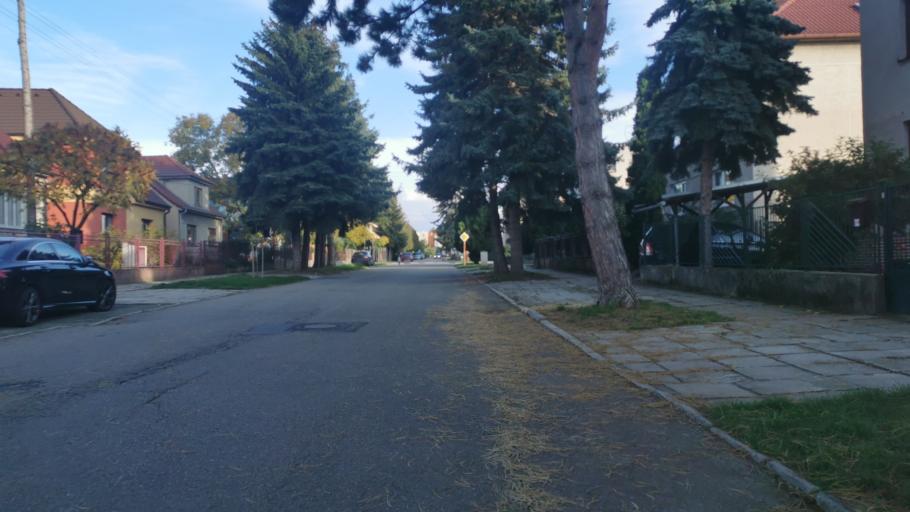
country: SK
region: Trnavsky
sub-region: Okres Skalica
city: Skalica
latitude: 48.8421
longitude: 17.2360
